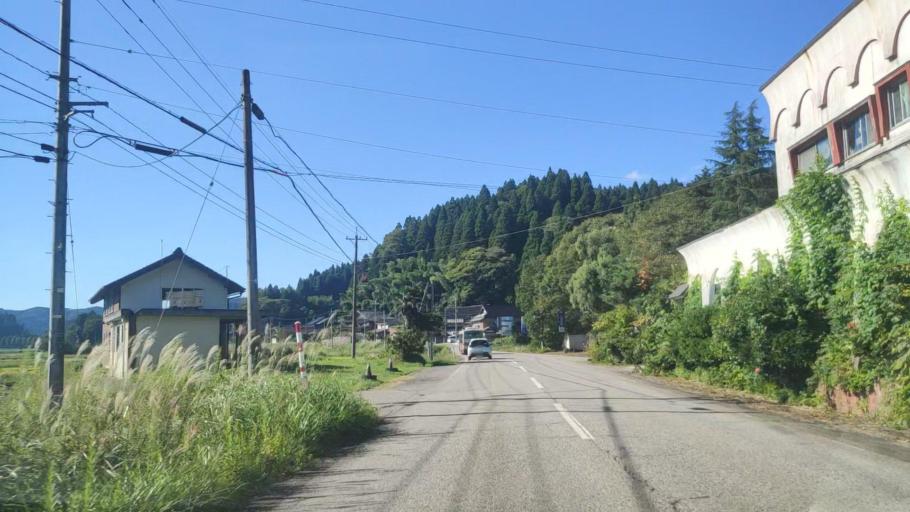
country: JP
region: Ishikawa
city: Nanao
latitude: 37.2771
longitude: 137.0526
